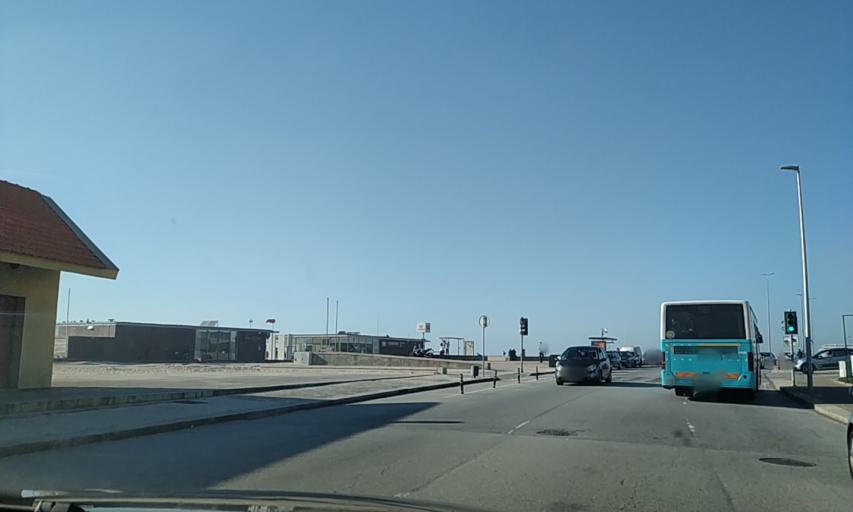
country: PT
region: Porto
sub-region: Matosinhos
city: Leca da Palmeira
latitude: 41.1891
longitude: -8.7043
